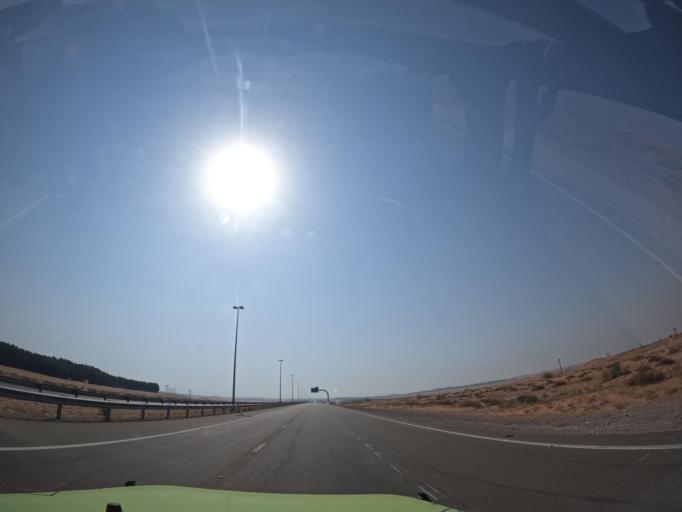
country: OM
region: Al Buraimi
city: Al Buraymi
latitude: 24.4149
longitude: 55.6965
